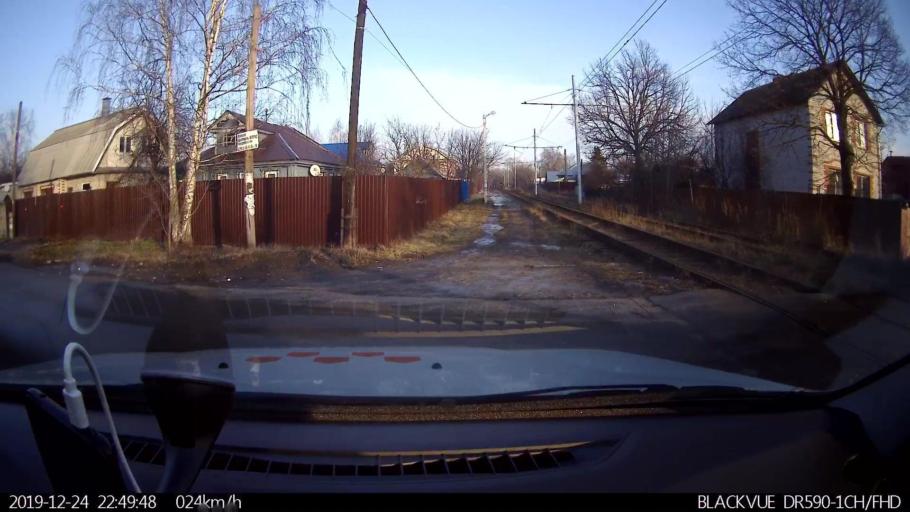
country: RU
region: Nizjnij Novgorod
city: Nizhniy Novgorod
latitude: 56.2878
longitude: 43.8999
